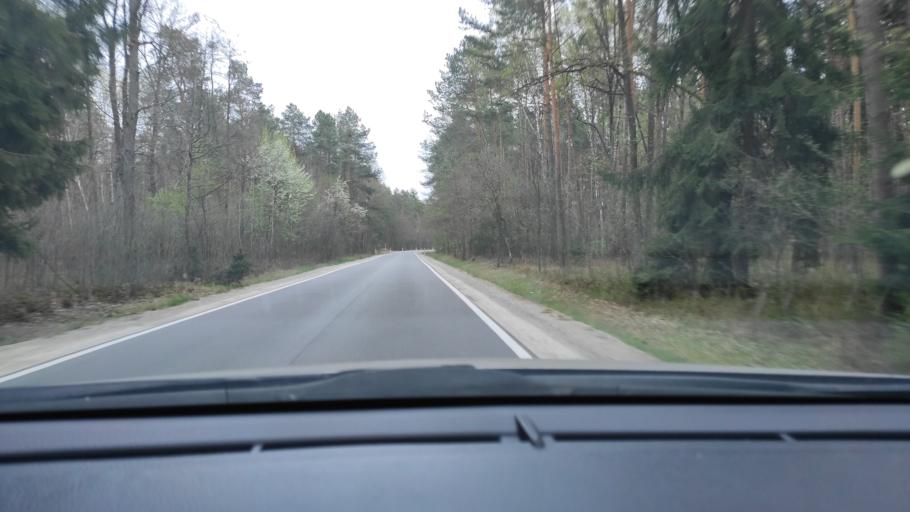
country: PL
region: Masovian Voivodeship
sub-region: Powiat zwolenski
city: Zwolen
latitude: 51.4046
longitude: 21.5316
